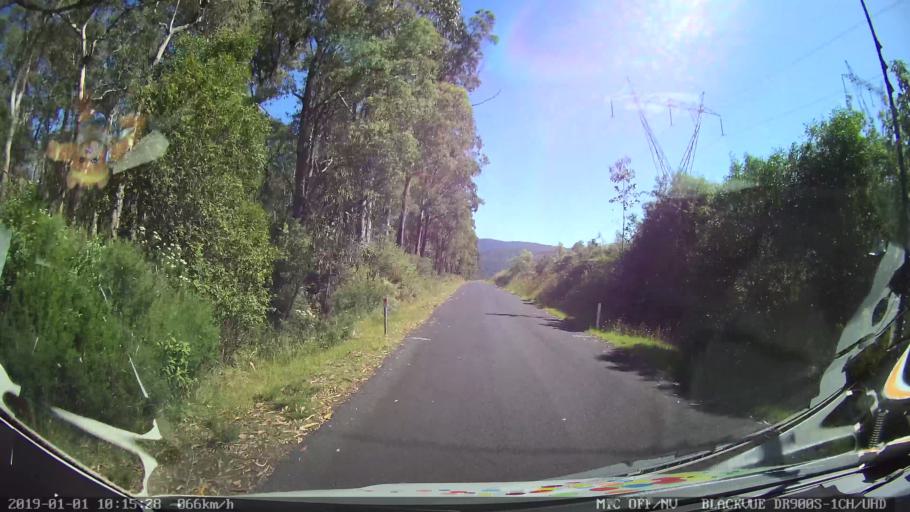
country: AU
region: New South Wales
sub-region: Snowy River
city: Jindabyne
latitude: -36.1014
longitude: 148.1620
